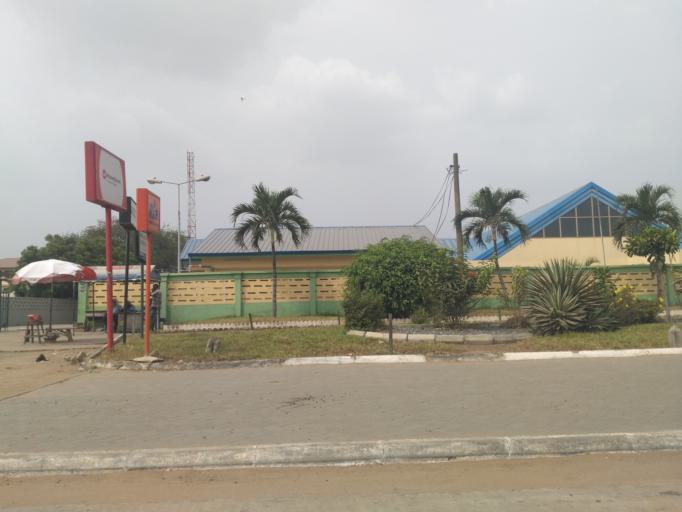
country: GH
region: Greater Accra
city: Accra
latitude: 5.5466
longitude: -0.2016
